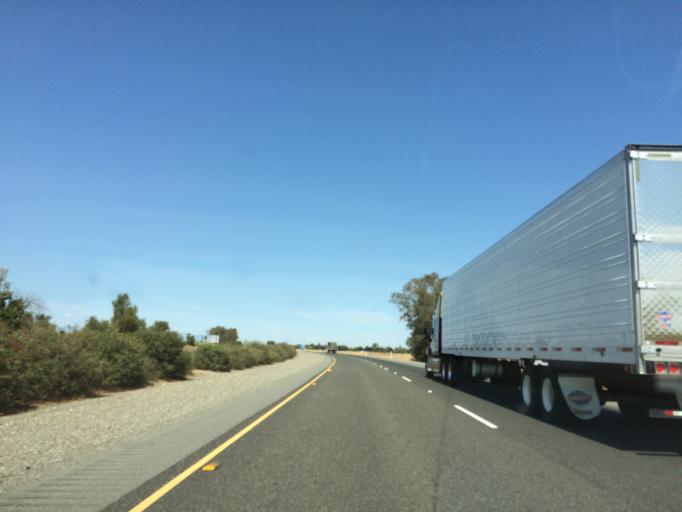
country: US
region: California
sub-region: Glenn County
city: Willows
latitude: 39.5006
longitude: -122.1998
